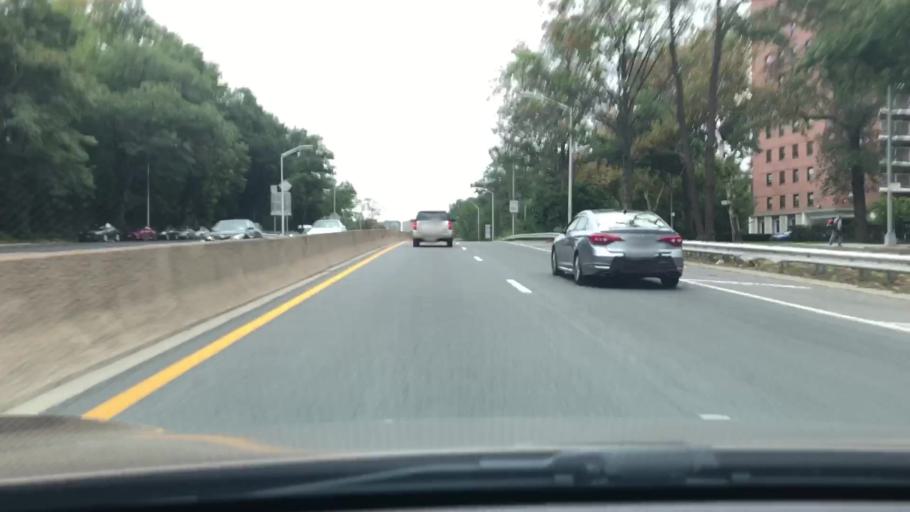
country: US
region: New York
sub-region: New York County
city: Inwood
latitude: 40.8960
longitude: -73.9081
